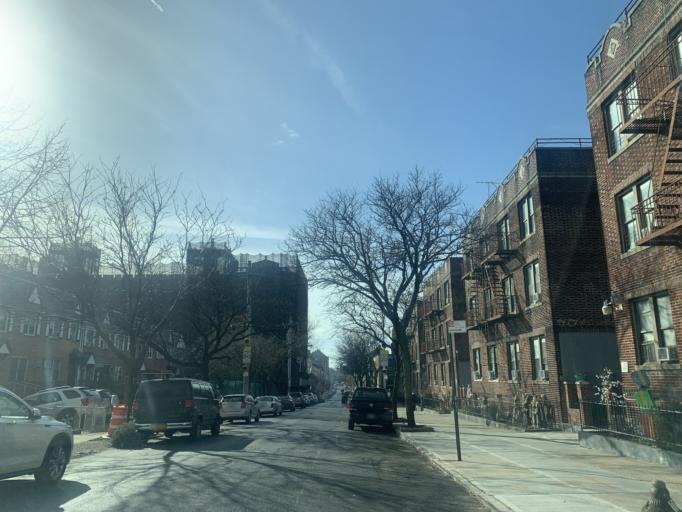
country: US
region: New York
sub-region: Queens County
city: Long Island City
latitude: 40.7078
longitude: -73.9193
